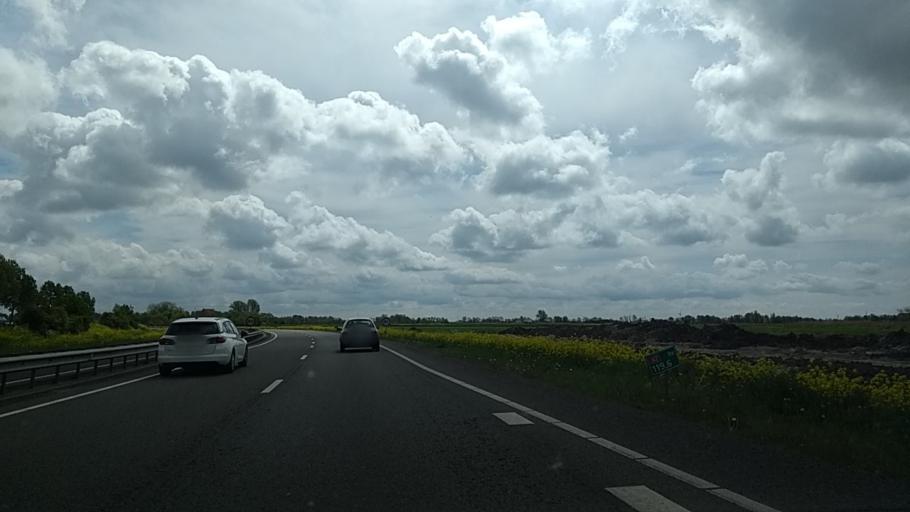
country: NL
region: Friesland
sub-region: Sudwest Fryslan
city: IJlst
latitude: 53.0293
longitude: 5.6256
